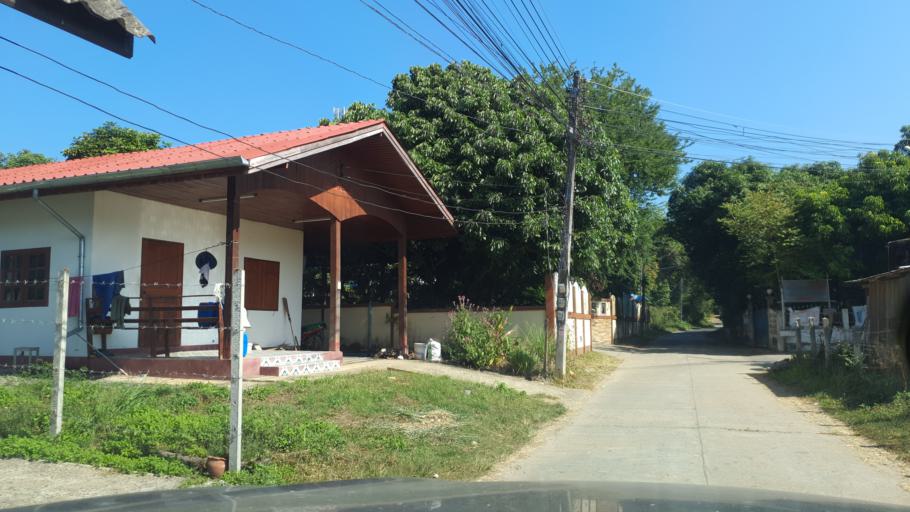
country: TH
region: Chiang Mai
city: San Sai
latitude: 18.8884
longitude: 99.1666
